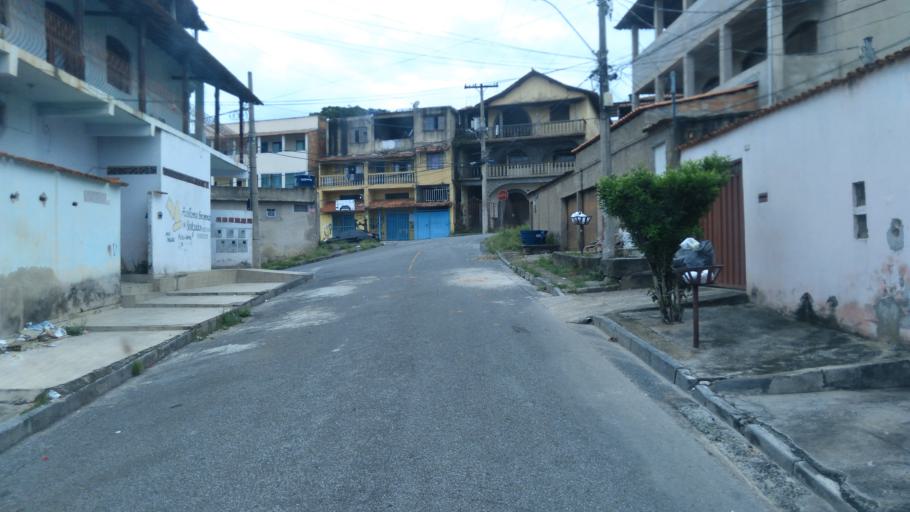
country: BR
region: Minas Gerais
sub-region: Belo Horizonte
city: Belo Horizonte
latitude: -19.8477
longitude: -43.9060
